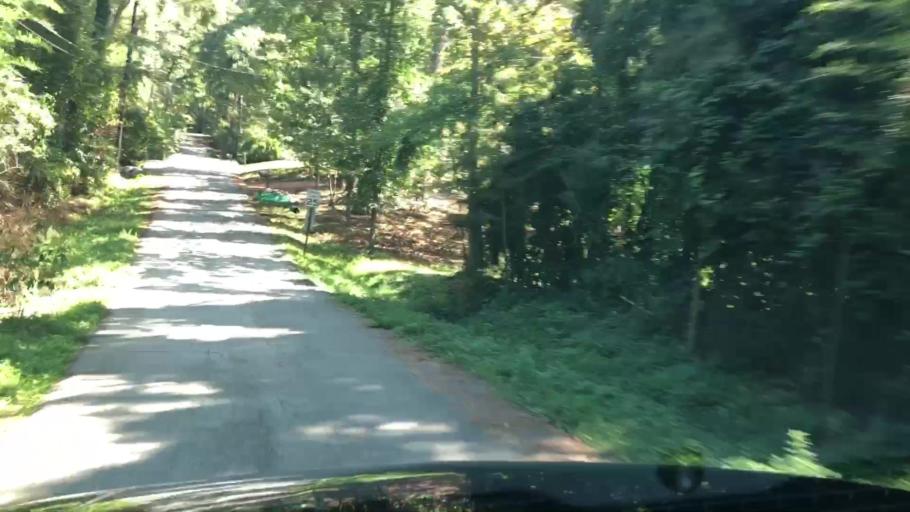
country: US
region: Georgia
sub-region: Paulding County
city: Dallas
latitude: 33.9275
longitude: -84.8367
